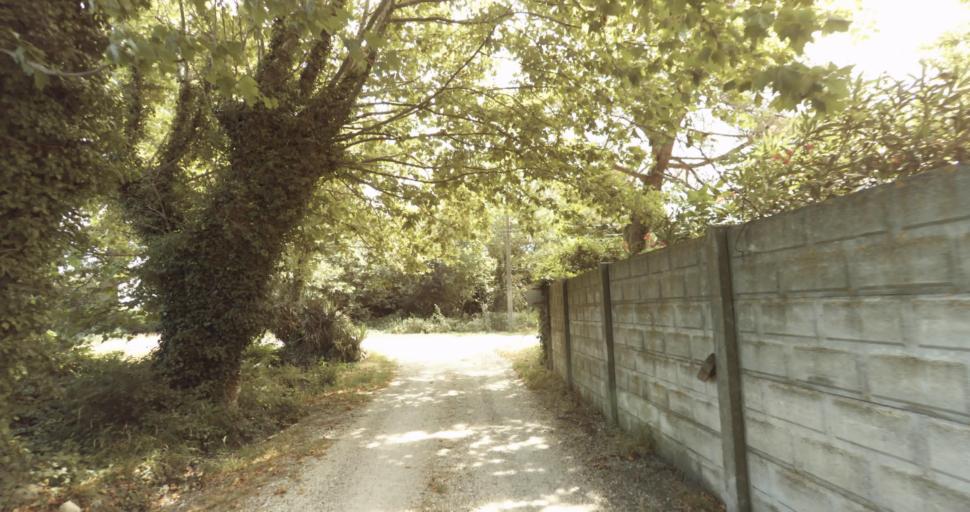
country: FR
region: Provence-Alpes-Cote d'Azur
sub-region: Departement du Vaucluse
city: Althen-des-Paluds
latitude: 44.0277
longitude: 4.9391
